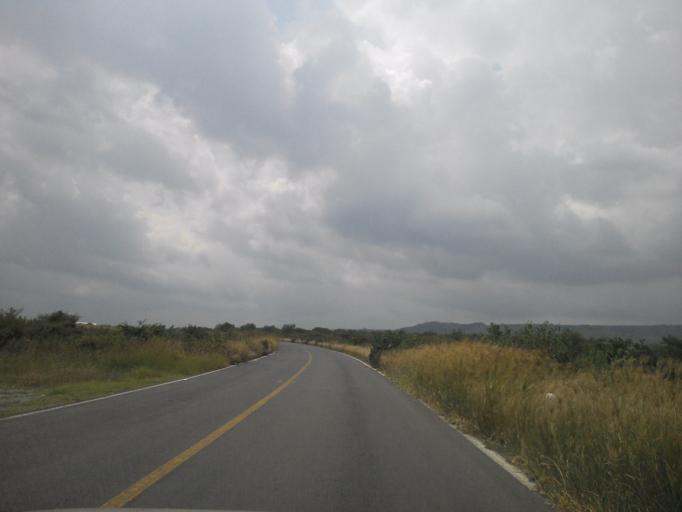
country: MX
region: Jalisco
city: San Diego de Alejandria
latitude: 20.9011
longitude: -102.0143
